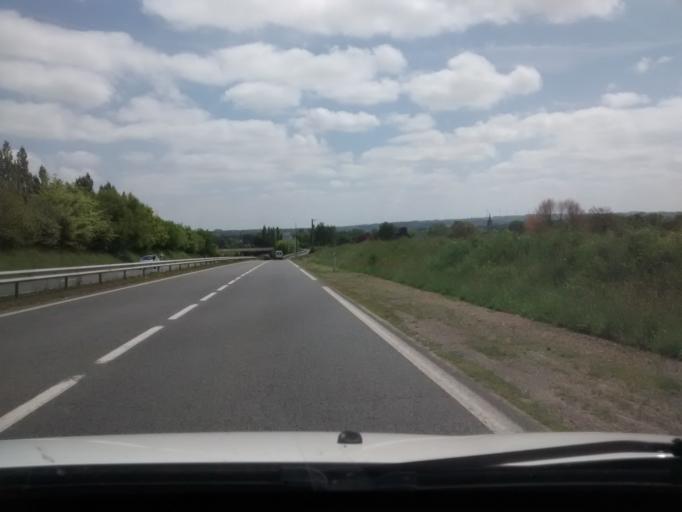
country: FR
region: Brittany
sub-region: Departement des Cotes-d'Armor
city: Pedernec
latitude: 48.6046
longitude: -3.2722
